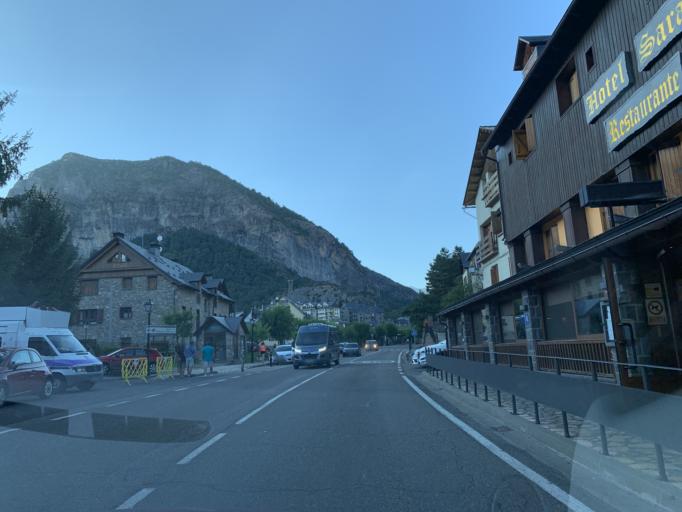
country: ES
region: Aragon
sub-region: Provincia de Huesca
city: Hoz de Jaca
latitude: 42.7332
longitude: -0.3118
